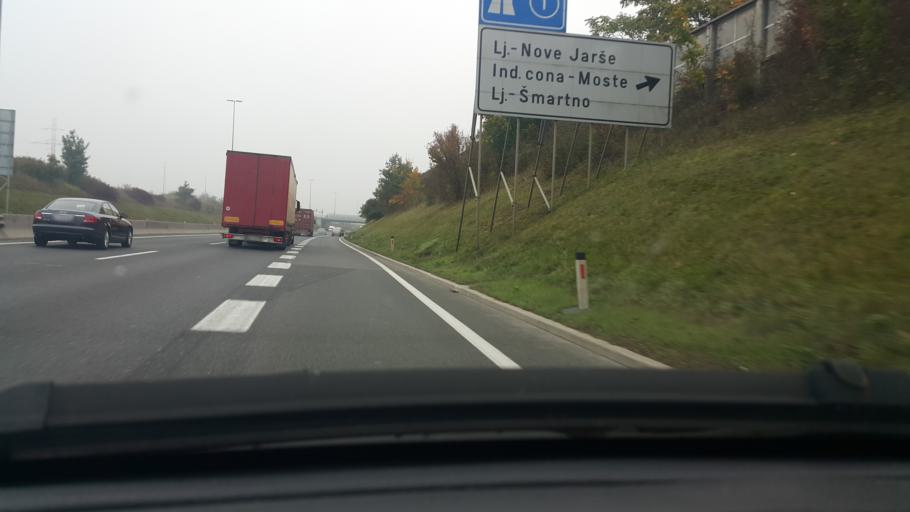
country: SI
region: Ljubljana
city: Ljubljana
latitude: 46.0745
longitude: 14.5449
